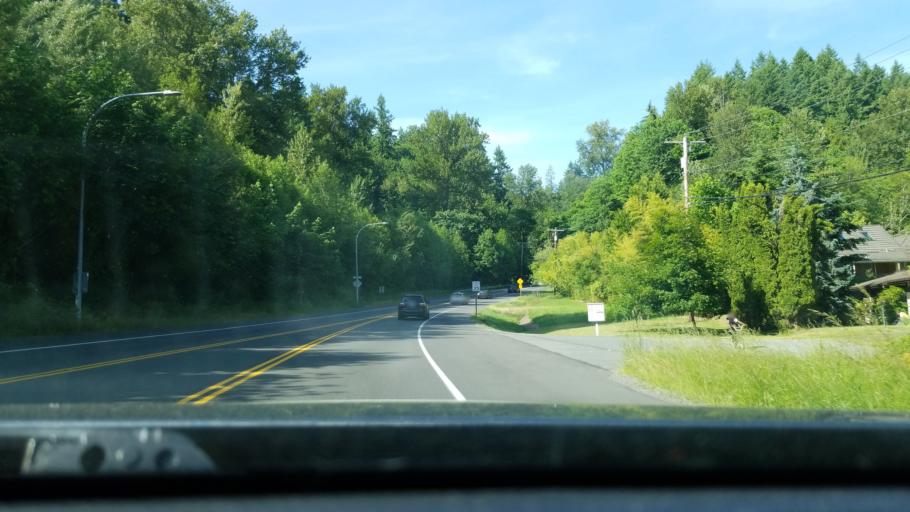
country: US
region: Washington
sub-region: King County
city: East Renton Highlands
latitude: 47.4688
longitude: -122.1363
